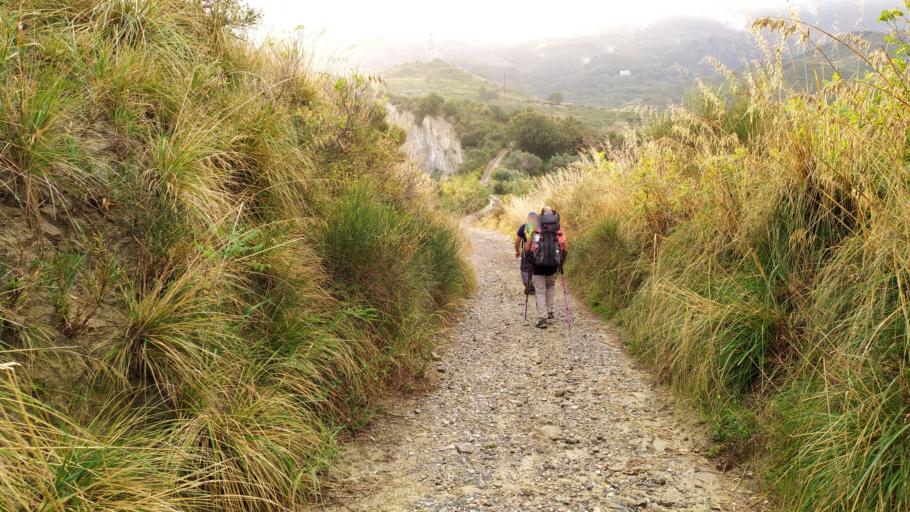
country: IT
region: Sicily
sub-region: Messina
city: Villafranca Tirrena
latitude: 38.2166
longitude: 15.4726
